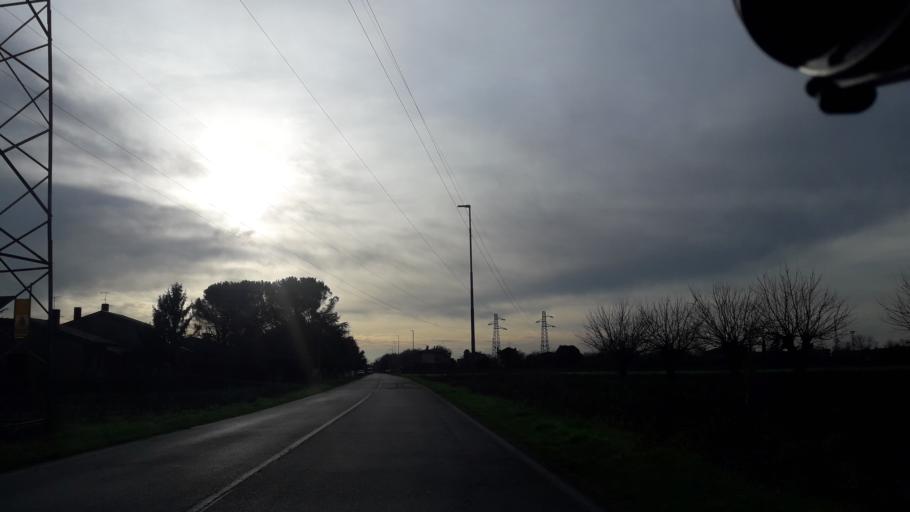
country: IT
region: Friuli Venezia Giulia
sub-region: Provincia di Udine
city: Udine
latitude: 46.0615
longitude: 13.2601
